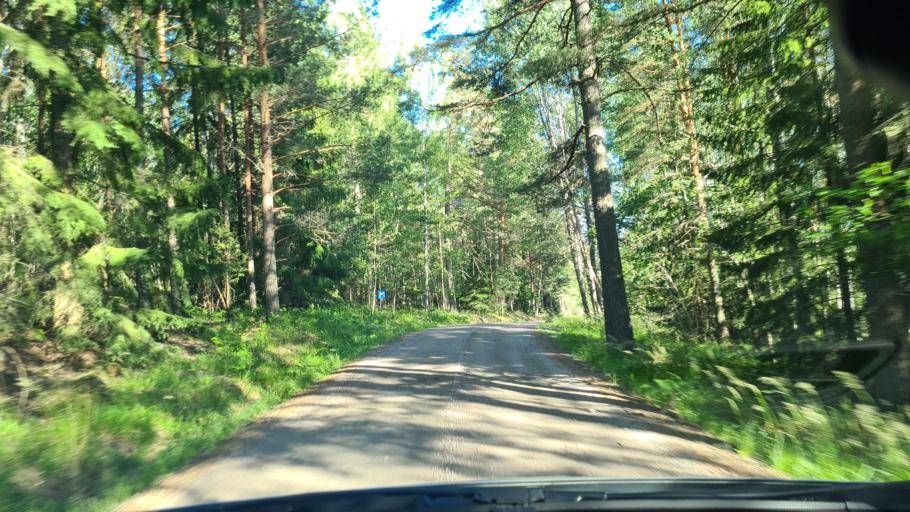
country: SE
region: Soedermanland
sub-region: Nykopings Kommun
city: Stigtomta
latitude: 58.9155
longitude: 16.9154
